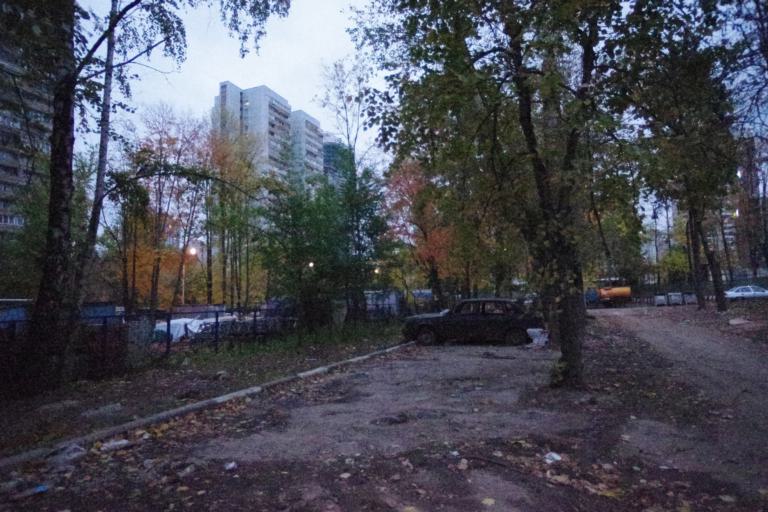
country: RU
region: Moscow
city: Troparevo
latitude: 55.6626
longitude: 37.5134
